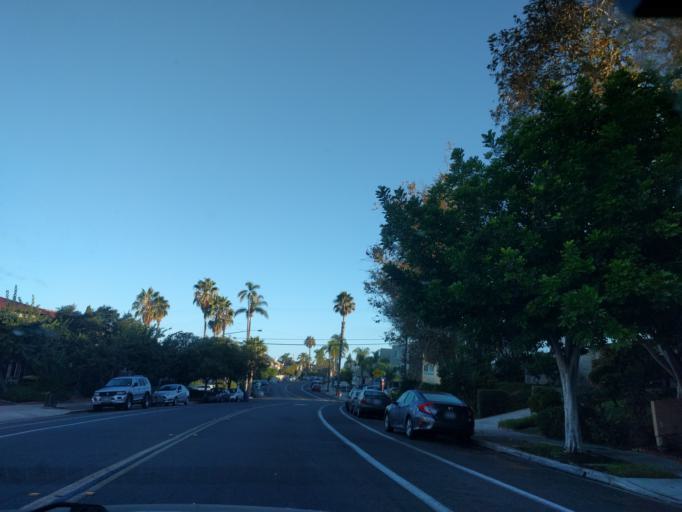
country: US
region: California
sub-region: San Diego County
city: San Diego
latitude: 32.7528
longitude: -117.1496
